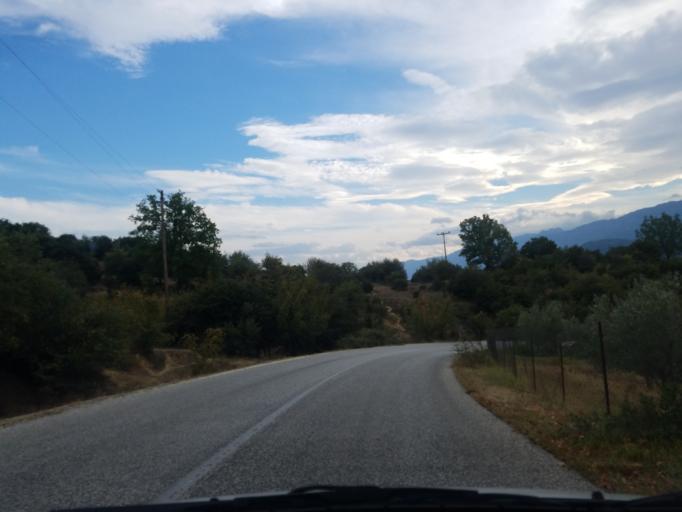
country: GR
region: Thessaly
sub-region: Trikala
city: Kalampaka
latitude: 39.7042
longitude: 21.6513
